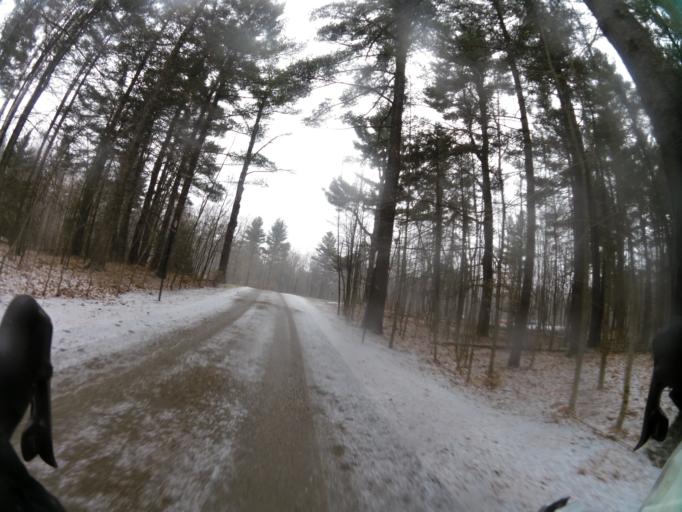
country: CA
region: Quebec
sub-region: Outaouais
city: Gatineau
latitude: 45.4853
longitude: -75.8453
